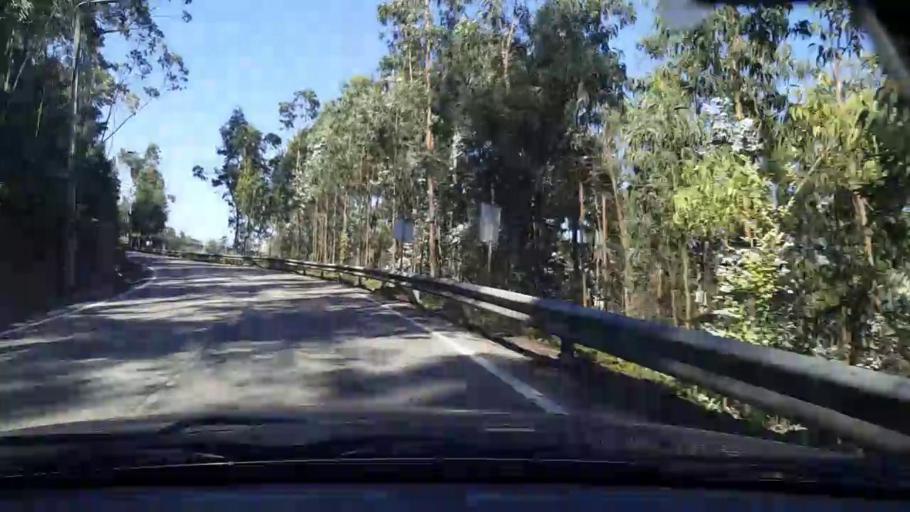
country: PT
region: Braga
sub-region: Vila Nova de Famalicao
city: Ribeirao
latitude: 41.3398
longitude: -8.6233
